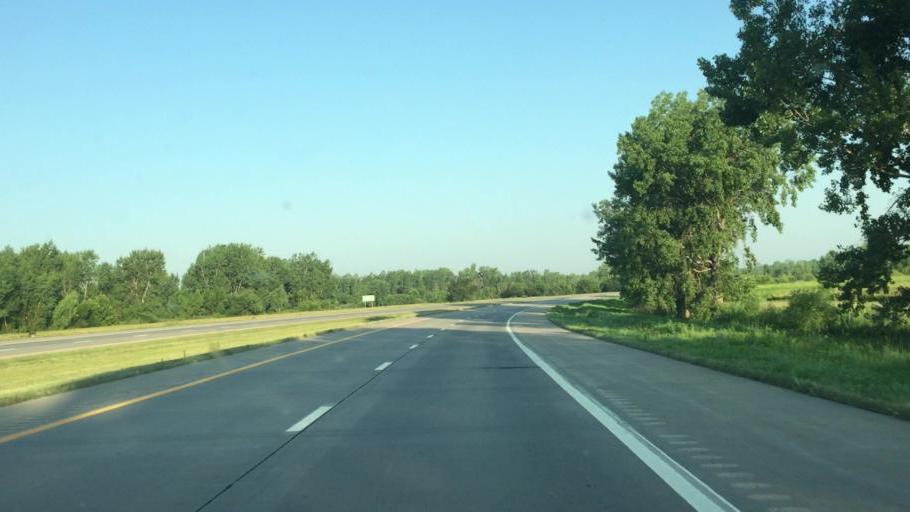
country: US
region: Kansas
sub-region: Doniphan County
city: Wathena
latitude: 39.7406
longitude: -94.9122
